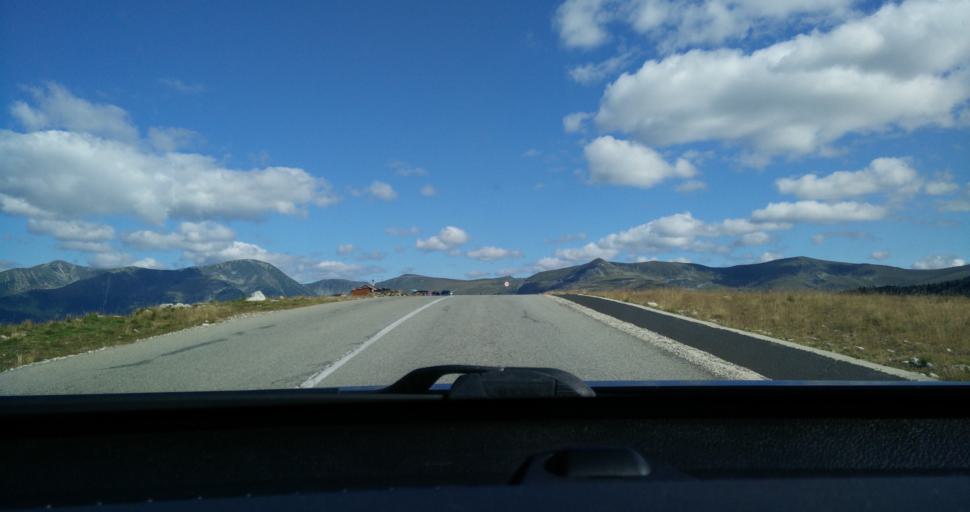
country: RO
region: Gorj
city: Novaci-Straini
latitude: 45.2643
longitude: 23.6842
